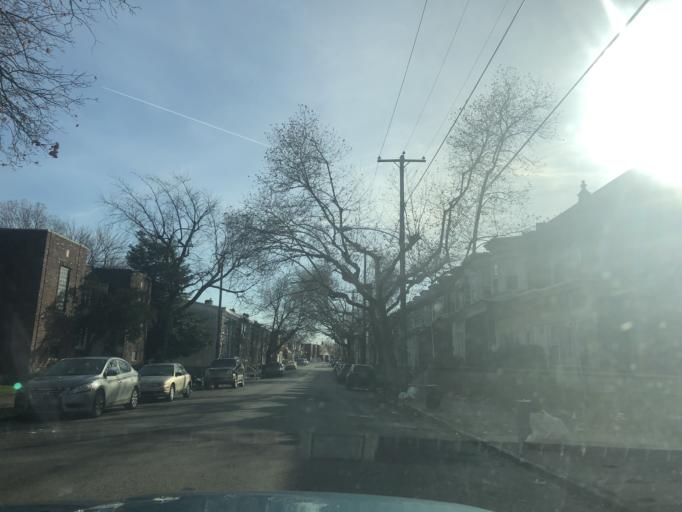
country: US
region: Pennsylvania
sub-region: Delaware County
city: Millbourne
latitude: 39.9687
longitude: -75.2304
